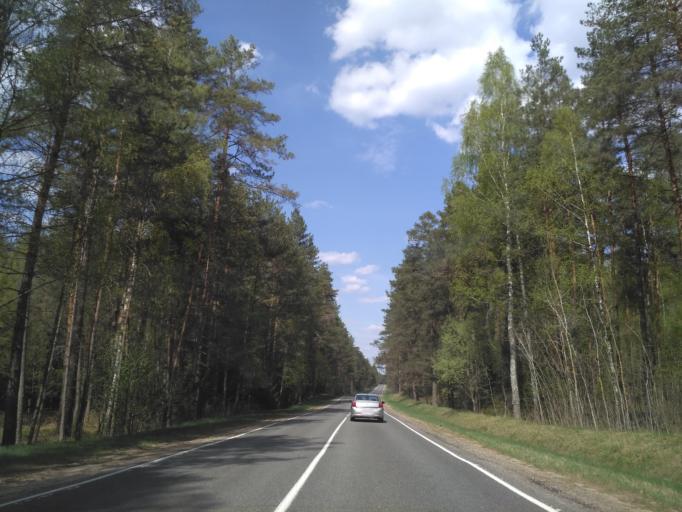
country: BY
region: Minsk
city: Myadzyel
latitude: 54.8039
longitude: 26.9409
